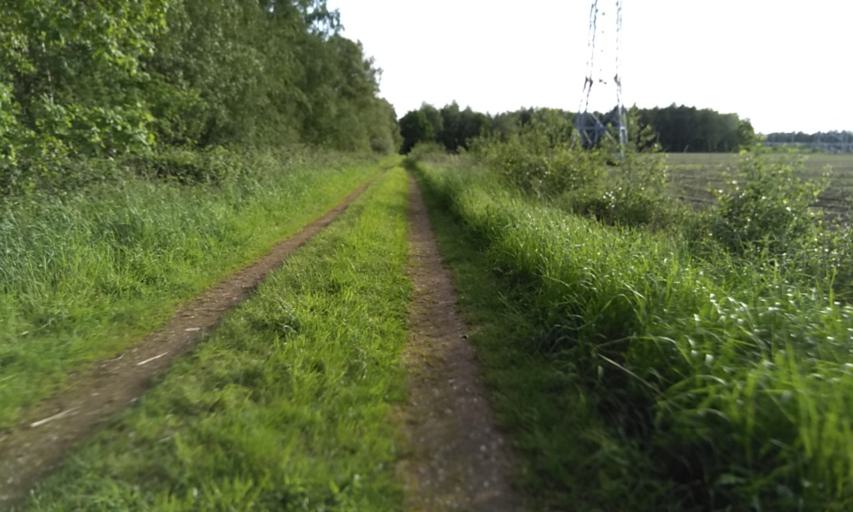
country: DE
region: Lower Saxony
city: Agathenburg
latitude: 53.5424
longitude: 9.5117
